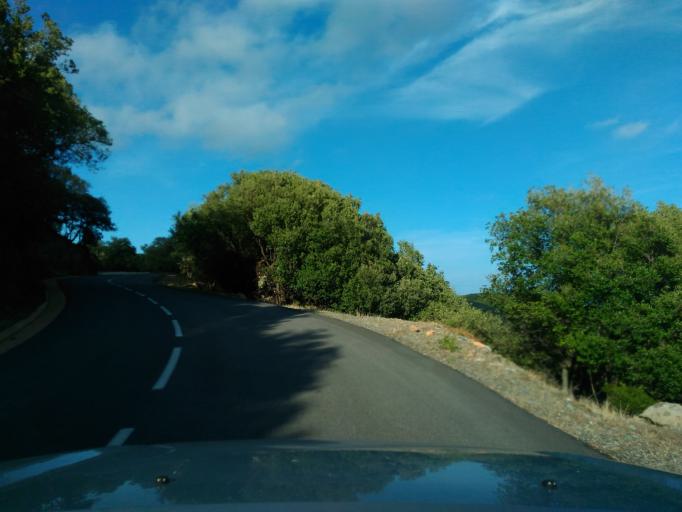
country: FR
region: Corsica
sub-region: Departement de la Haute-Corse
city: Brando
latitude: 42.9609
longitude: 9.4280
